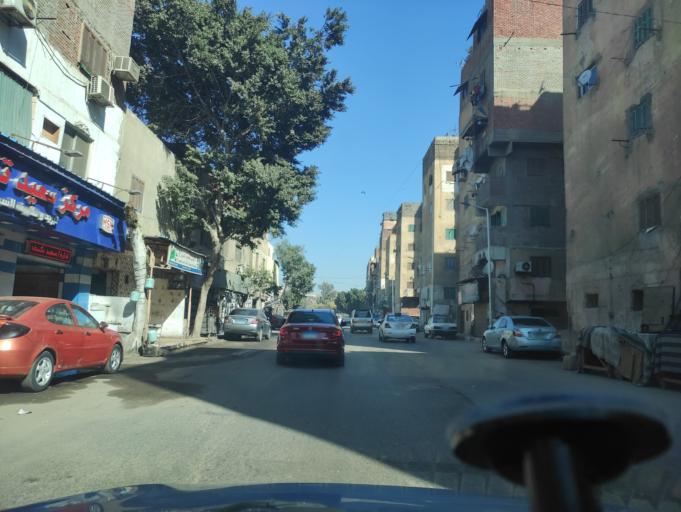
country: EG
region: Muhafazat al Qahirah
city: Cairo
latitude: 30.0223
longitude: 31.2640
